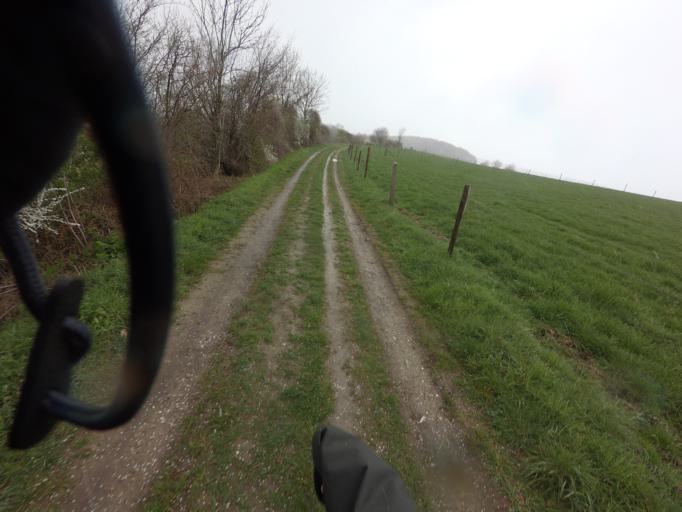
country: NL
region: Limburg
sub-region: Valkenburg aan de Geul
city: Schin op Geul
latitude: 50.8409
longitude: 5.8673
